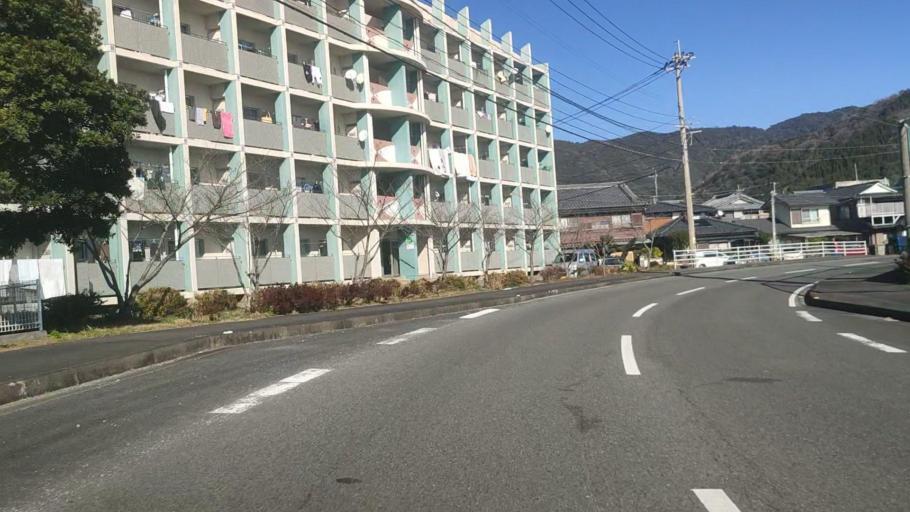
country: JP
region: Oita
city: Saiki
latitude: 32.8008
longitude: 131.9200
